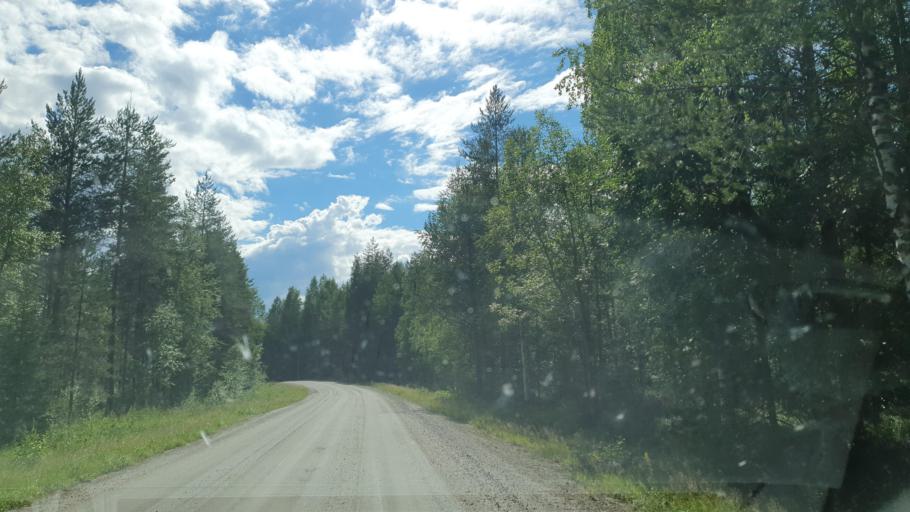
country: FI
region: Kainuu
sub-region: Kehys-Kainuu
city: Kuhmo
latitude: 64.1437
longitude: 29.7044
